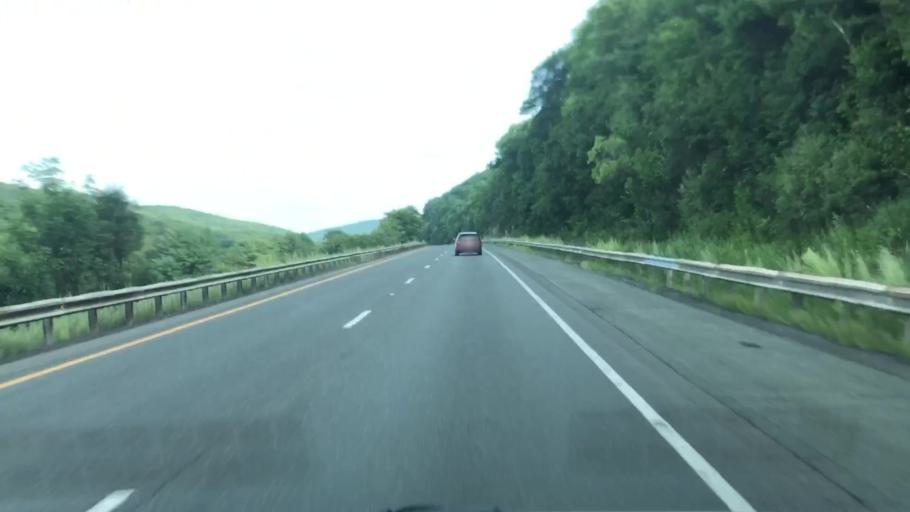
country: US
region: Massachusetts
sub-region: Berkshire County
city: Becket
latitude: 42.2703
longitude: -73.1330
